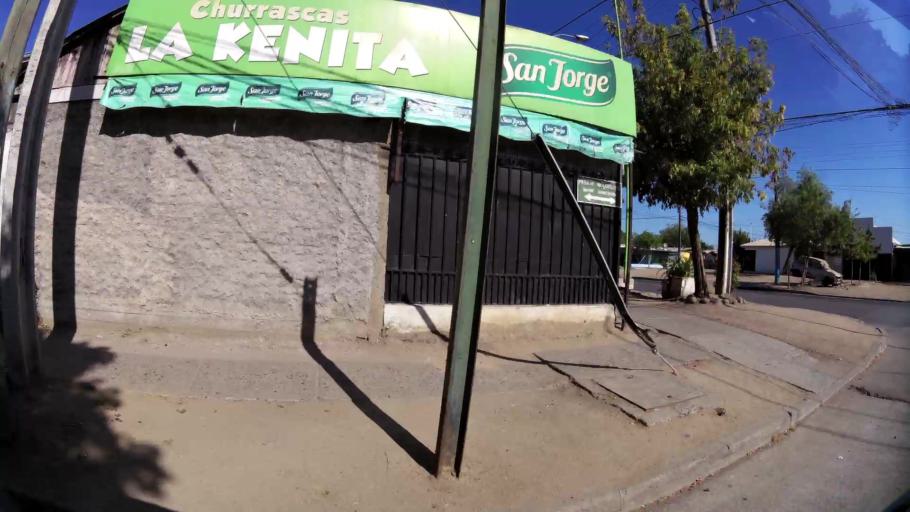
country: CL
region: Maule
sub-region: Provincia de Talca
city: Talca
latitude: -35.4460
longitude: -71.6530
